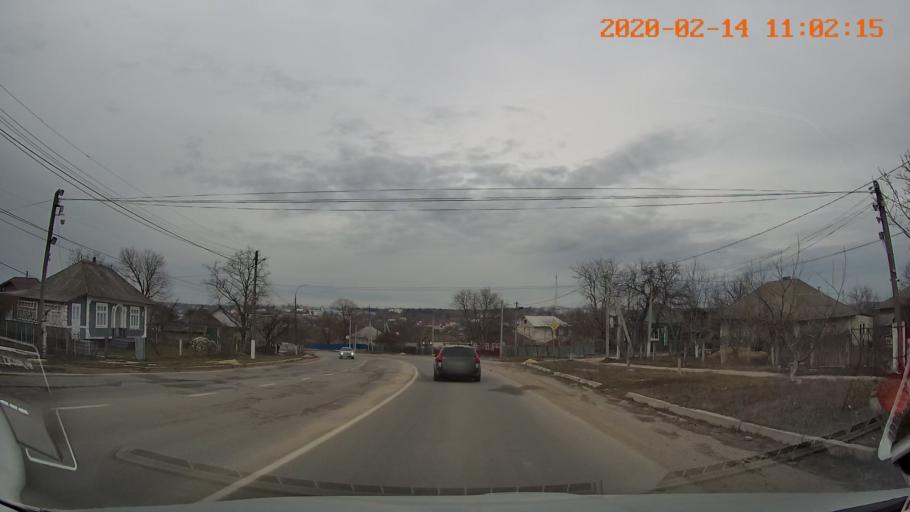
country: MD
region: Raionul Edinet
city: Edinet
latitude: 48.1636
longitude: 27.3214
